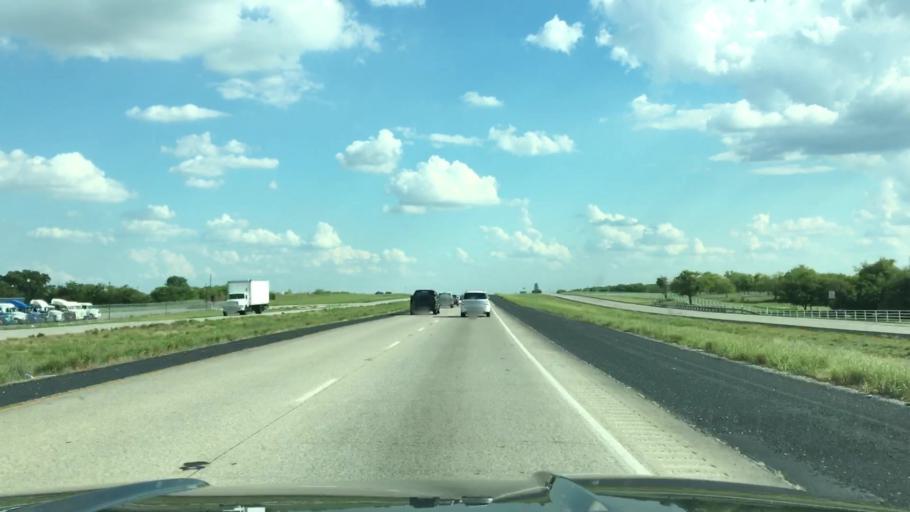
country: US
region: Texas
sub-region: Wise County
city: Rhome
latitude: 33.0209
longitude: -97.4422
